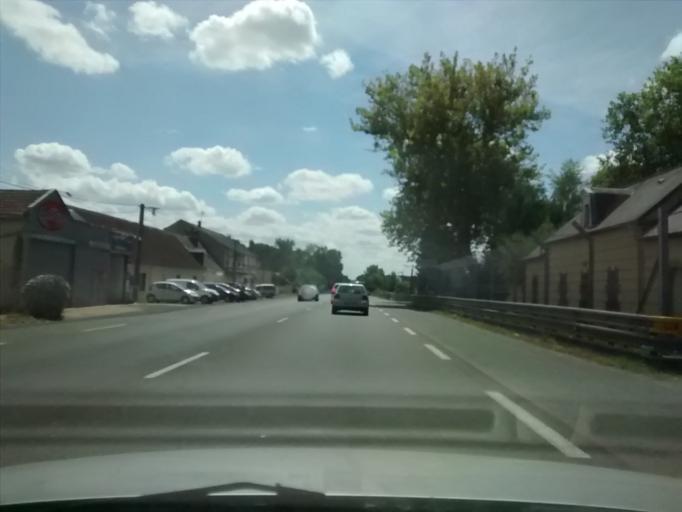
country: FR
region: Pays de la Loire
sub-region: Departement de la Sarthe
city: Ruaudin
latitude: 47.9487
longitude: 0.2314
